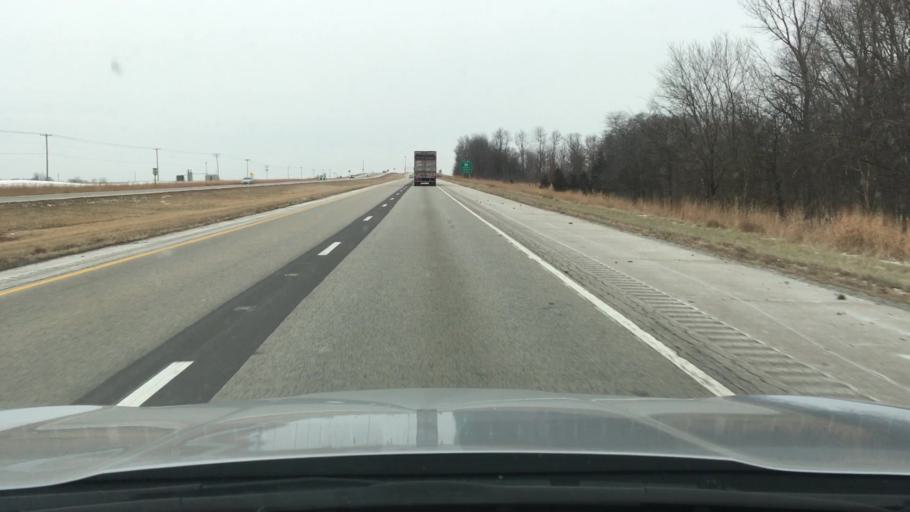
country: US
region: Illinois
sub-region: Sangamon County
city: Divernon
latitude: 39.5813
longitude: -89.6462
